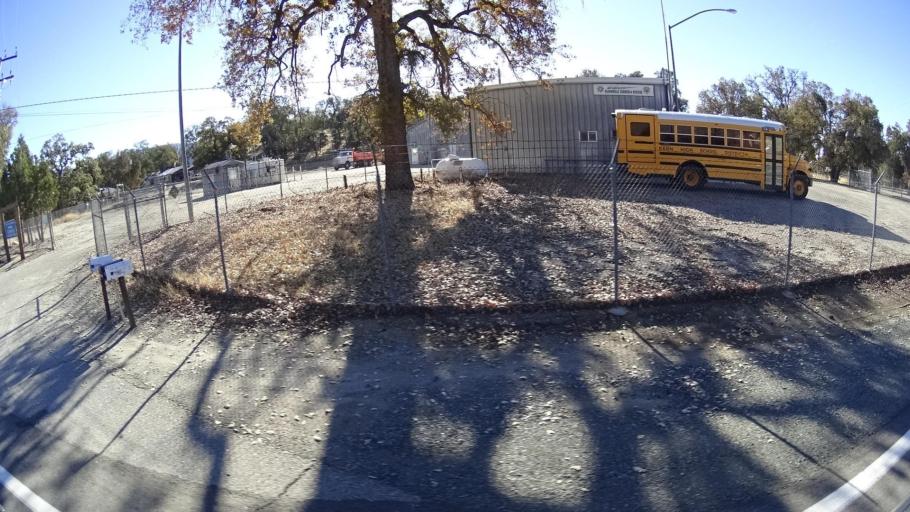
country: US
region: California
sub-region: Kern County
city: Alta Sierra
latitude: 35.7183
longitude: -118.7266
